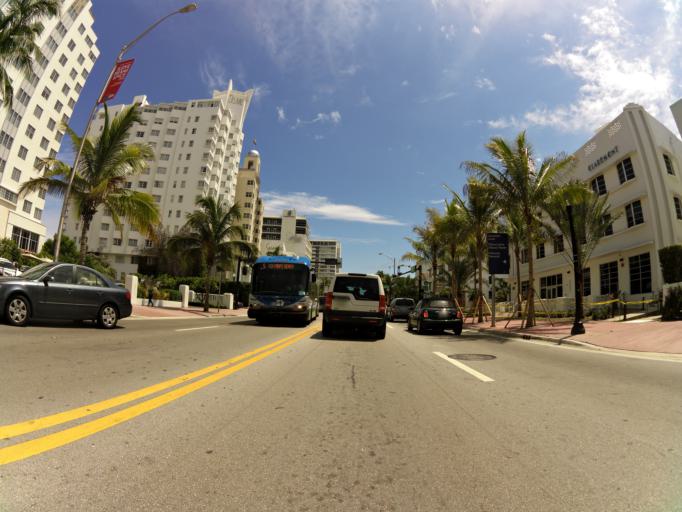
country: US
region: Florida
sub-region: Miami-Dade County
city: Miami Beach
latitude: 25.7927
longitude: -80.1297
